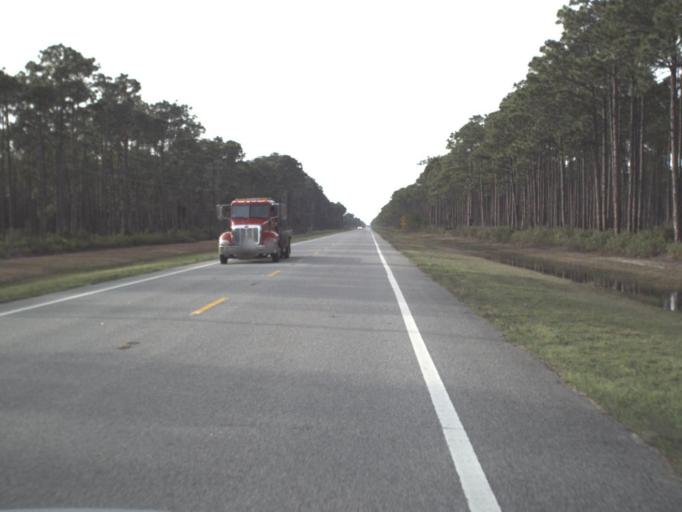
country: US
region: Florida
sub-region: Bay County
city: Tyndall Air Force Base
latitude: 30.0250
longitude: -85.5318
